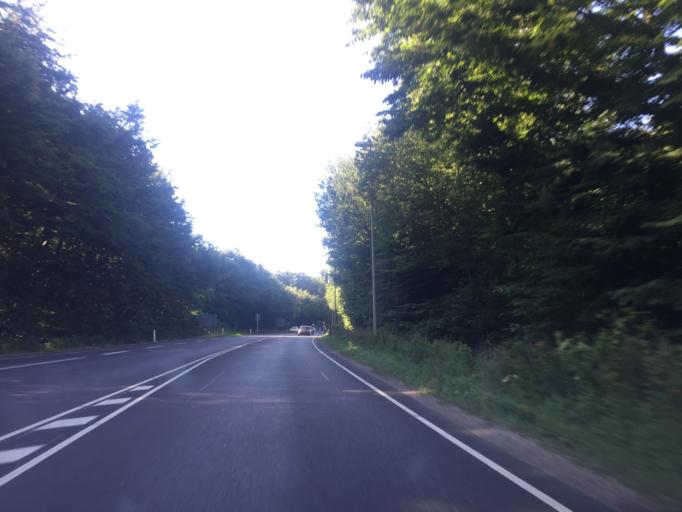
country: DK
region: Zealand
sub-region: Guldborgsund Kommune
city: Nykobing Falster
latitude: 54.7912
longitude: 11.8727
